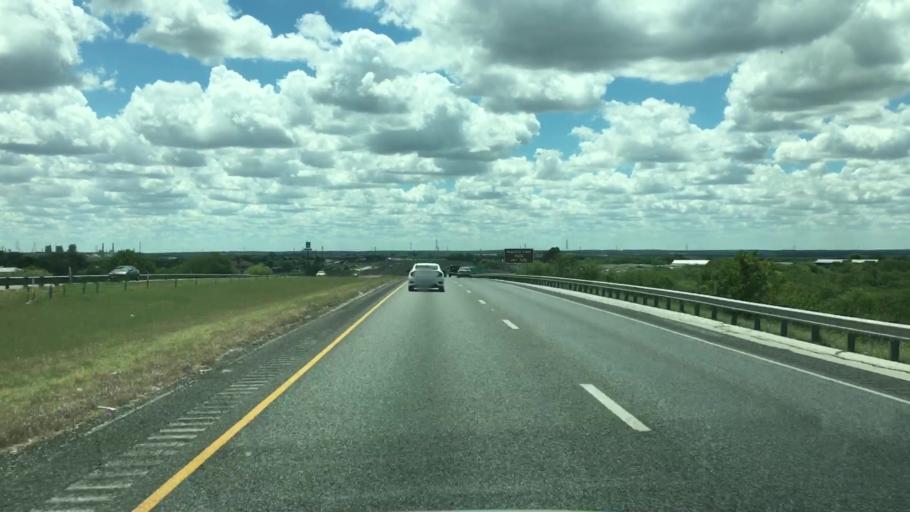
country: US
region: Texas
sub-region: Bexar County
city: Elmendorf
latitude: 29.2892
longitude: -98.3955
